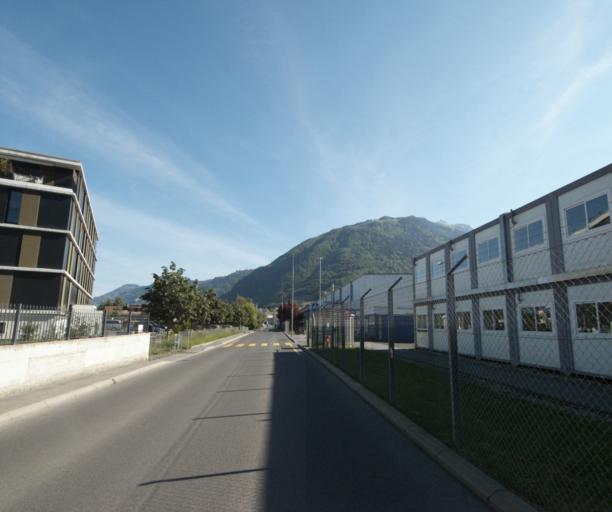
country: CH
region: Vaud
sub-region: Aigle District
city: Villeneuve
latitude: 46.3906
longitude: 6.9295
